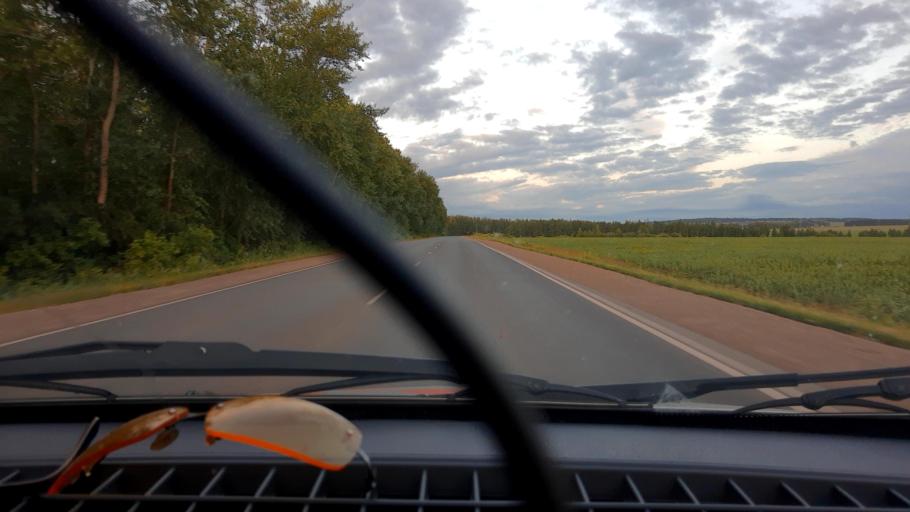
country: RU
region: Bashkortostan
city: Avdon
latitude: 54.5859
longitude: 55.7952
